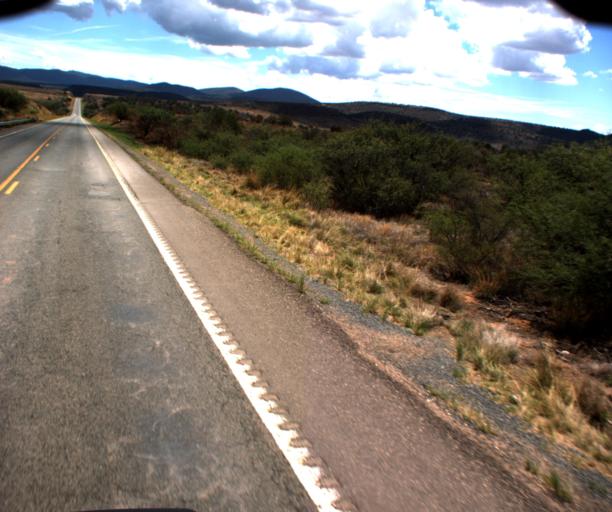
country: US
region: Arizona
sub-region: Yavapai County
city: Verde Village
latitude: 34.5221
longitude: -112.0418
